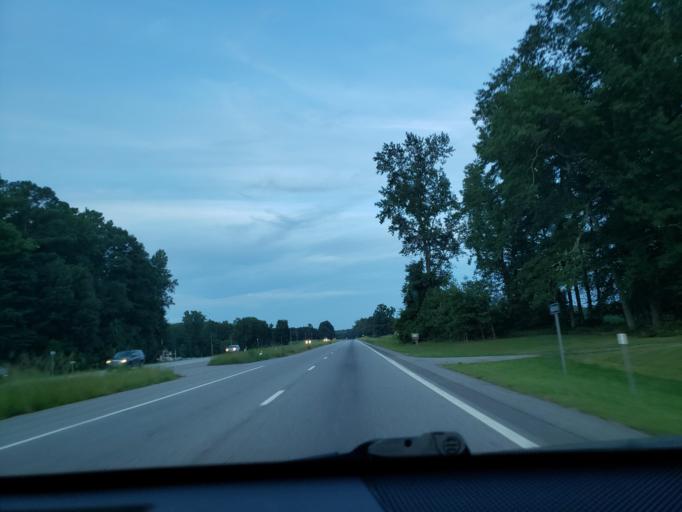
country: US
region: Virginia
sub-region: Southampton County
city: Courtland
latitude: 36.7063
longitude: -77.1805
